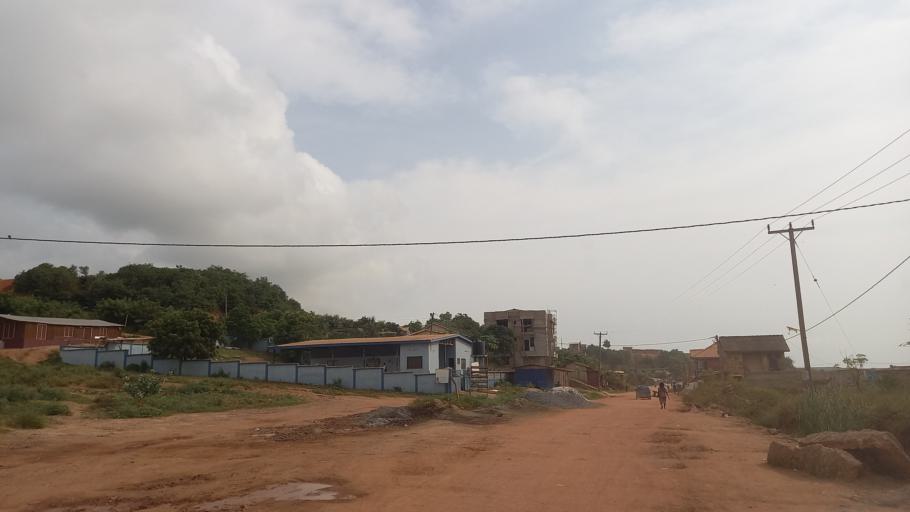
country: GH
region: Western
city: Shama Junction
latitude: 4.9761
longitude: -1.6479
